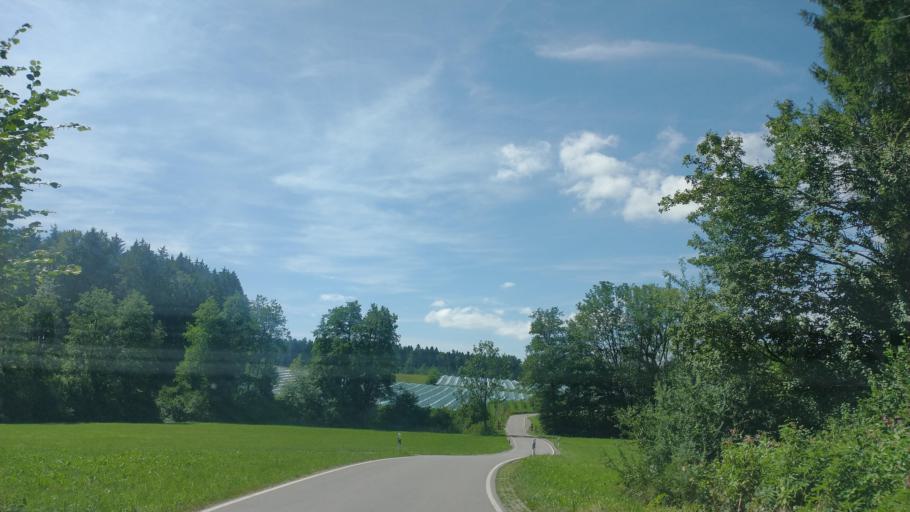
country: DE
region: Baden-Wuerttemberg
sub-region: Tuebingen Region
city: Neukirch
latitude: 47.6531
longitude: 9.6491
